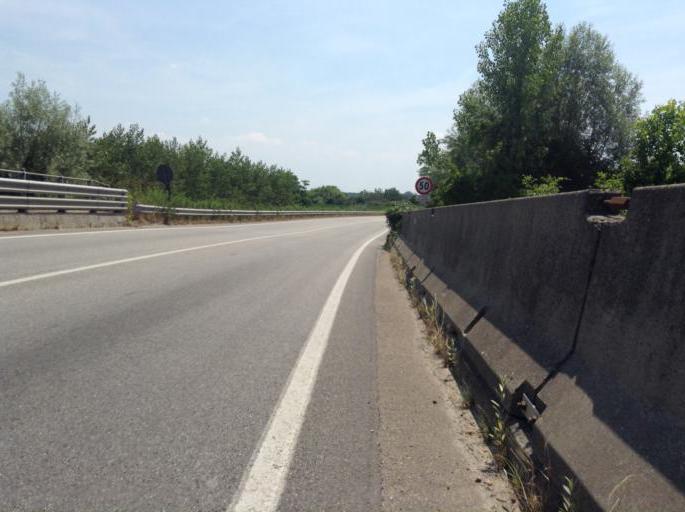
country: IT
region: Piedmont
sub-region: Provincia di Torino
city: Carignano
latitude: 44.9144
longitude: 7.6791
